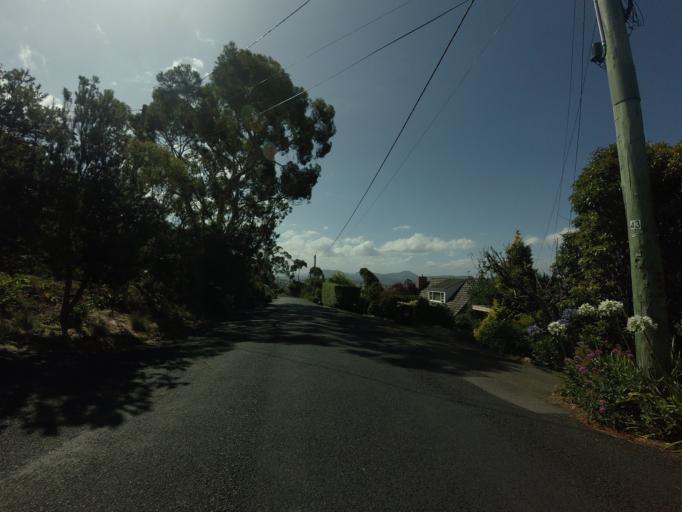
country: AU
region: Tasmania
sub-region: Hobart
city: Dynnyrne
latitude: -42.9123
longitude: 147.3268
